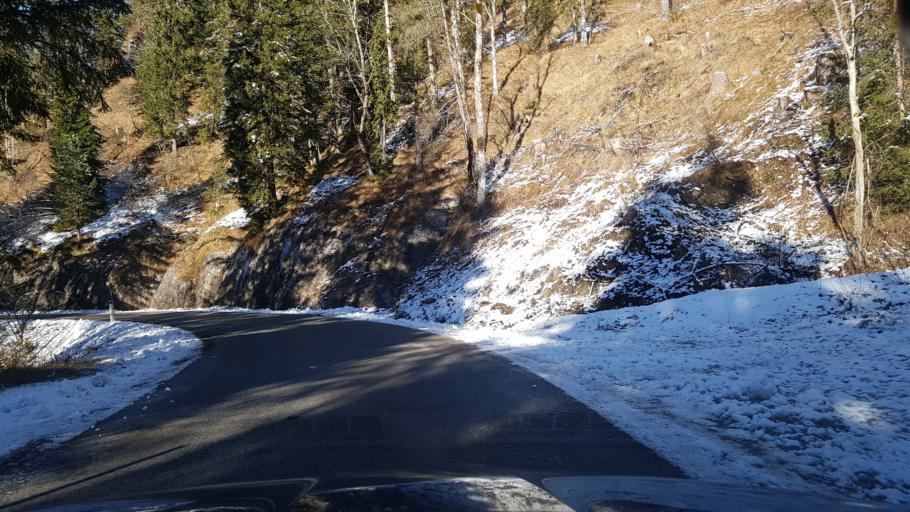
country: AT
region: Salzburg
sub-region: Politischer Bezirk Salzburg-Umgebung
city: Faistenau
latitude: 47.7677
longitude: 13.2271
